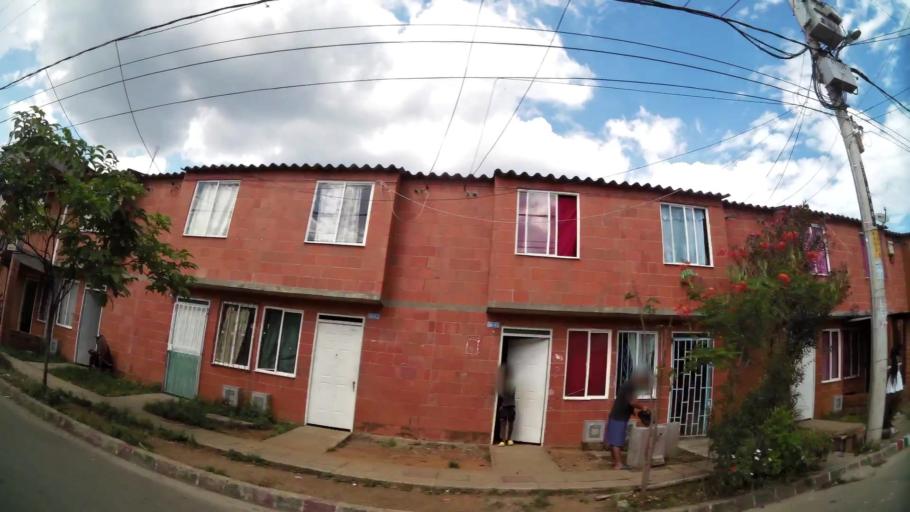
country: CO
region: Valle del Cauca
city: Cali
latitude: 3.3948
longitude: -76.5067
